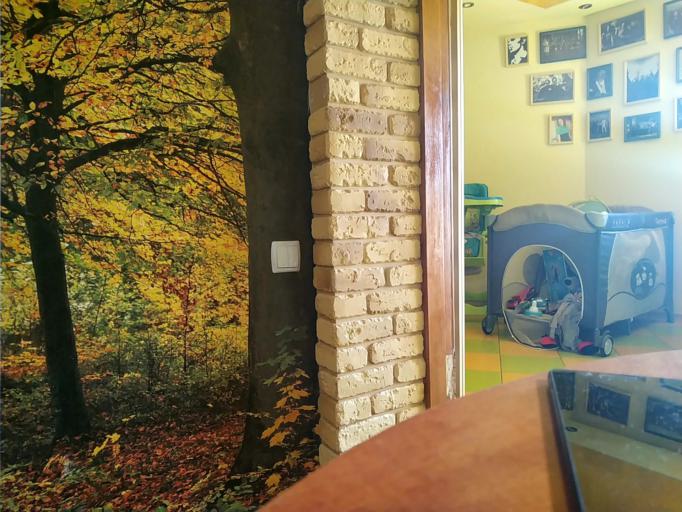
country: RU
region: Tverskaya
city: Vyshniy Volochek
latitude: 57.5195
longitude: 34.6297
